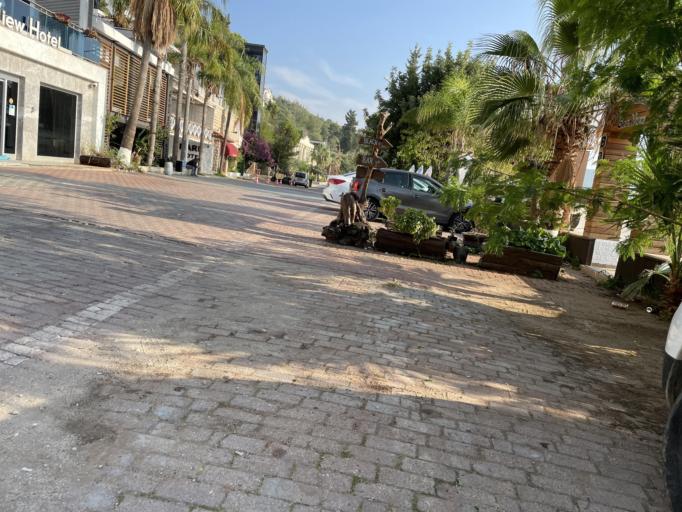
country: TR
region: Antalya
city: Kas
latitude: 36.1971
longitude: 29.6449
